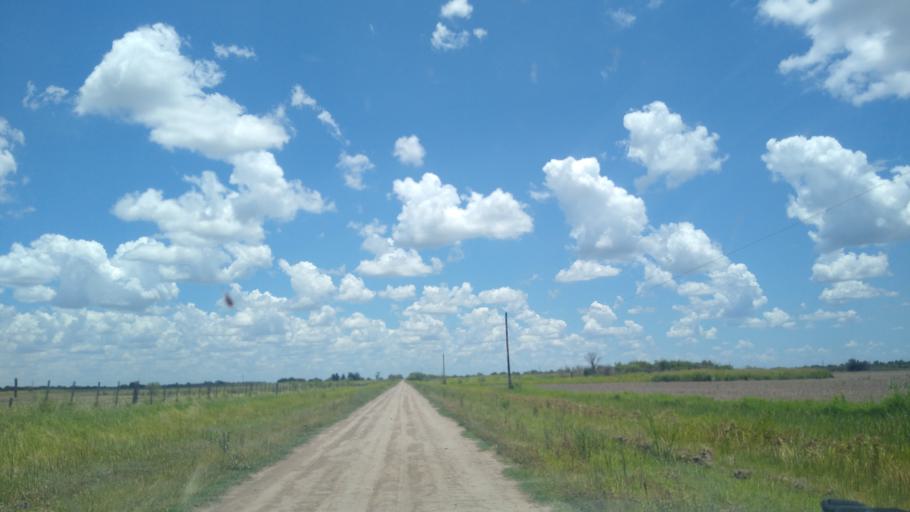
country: AR
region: Chaco
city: Presidencia Roque Saenz Pena
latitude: -26.7348
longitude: -60.3746
